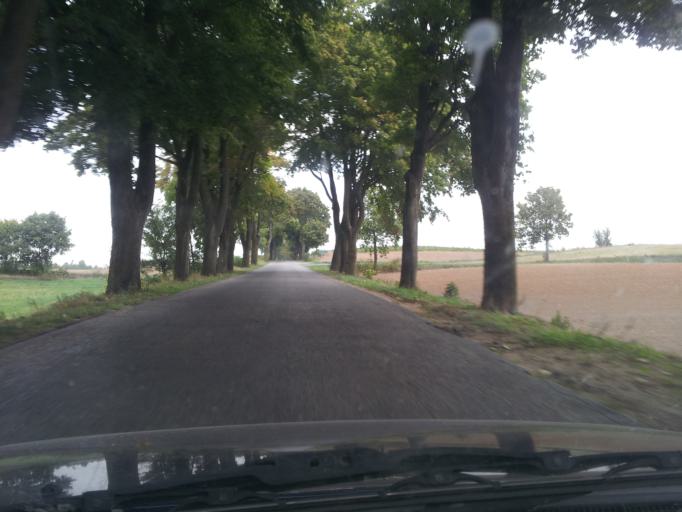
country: PL
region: Kujawsko-Pomorskie
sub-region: Powiat brodnicki
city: Brzozie
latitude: 53.3801
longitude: 19.6806
